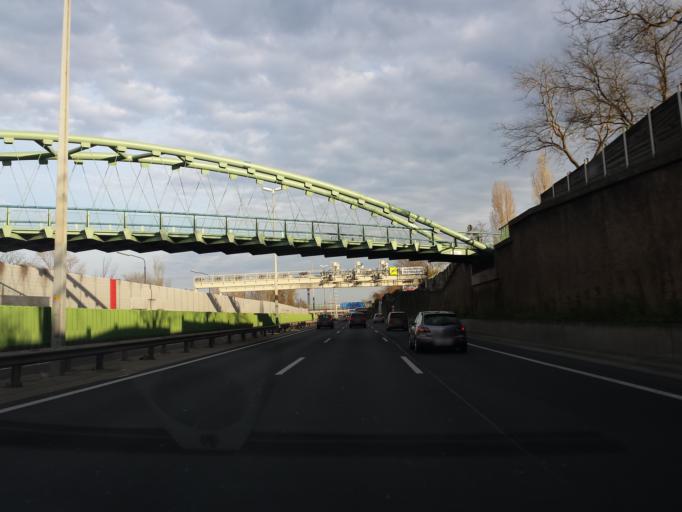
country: AT
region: Vienna
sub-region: Wien Stadt
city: Vienna
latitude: 48.2158
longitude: 16.4336
